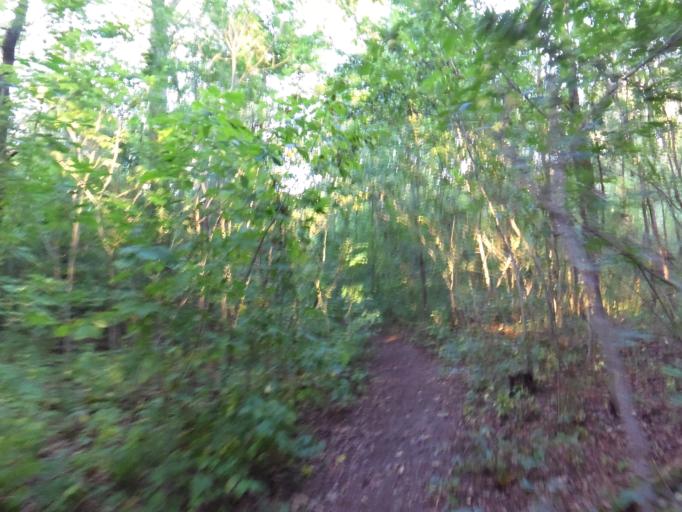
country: DE
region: Saxony
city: Leipzig
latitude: 51.3453
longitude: 12.3289
